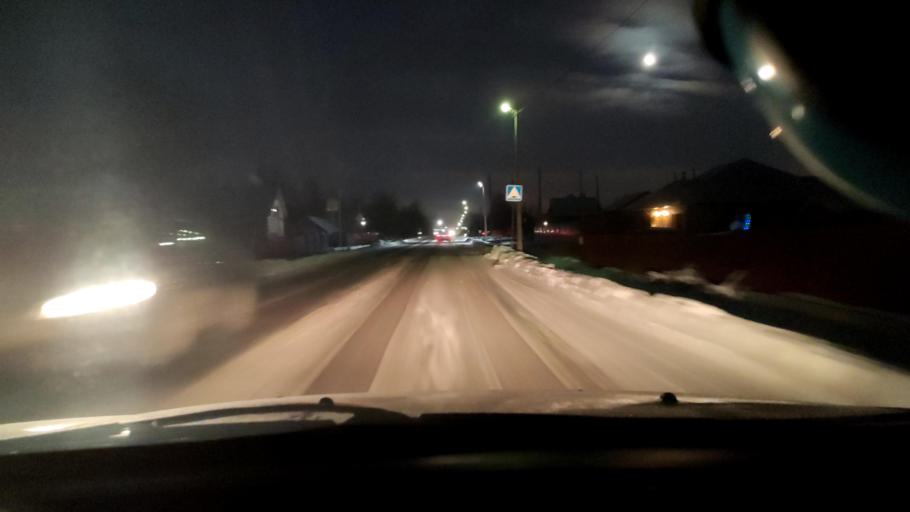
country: RU
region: Perm
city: Kultayevo
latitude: 57.8978
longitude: 55.9530
